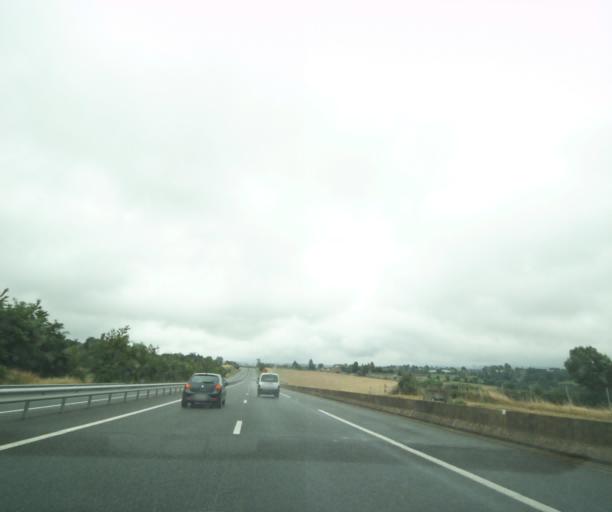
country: FR
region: Midi-Pyrenees
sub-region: Departement de l'Aveyron
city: Luc-la-Primaube
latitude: 44.3103
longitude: 2.5402
